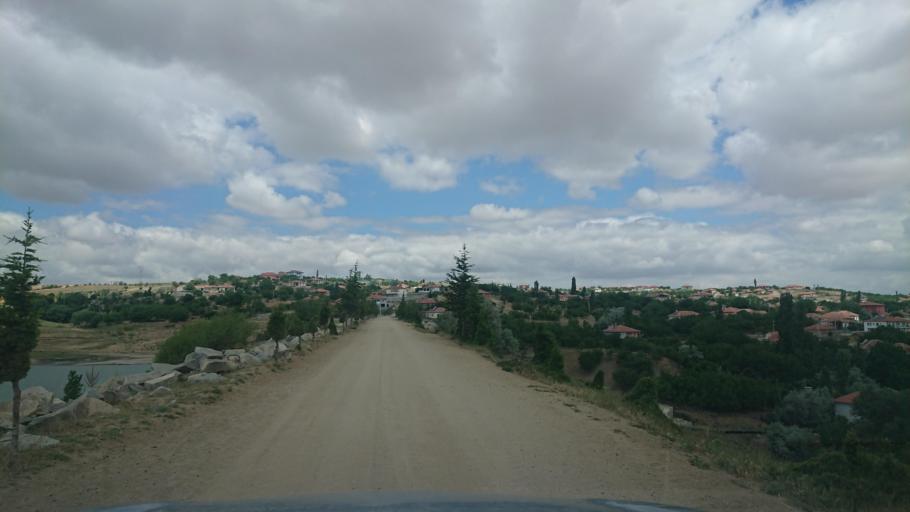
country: TR
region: Aksaray
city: Agacoren
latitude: 38.8651
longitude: 33.9508
